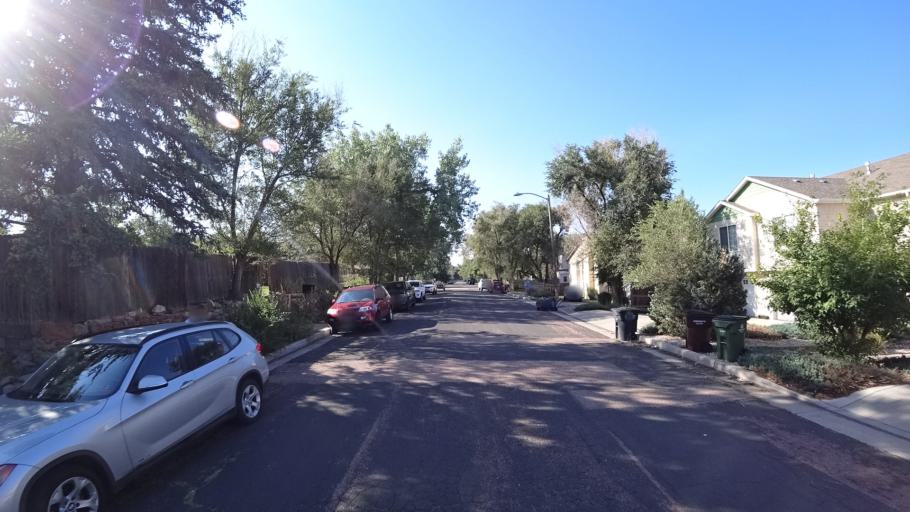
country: US
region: Colorado
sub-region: El Paso County
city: Colorado Springs
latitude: 38.8745
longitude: -104.8296
